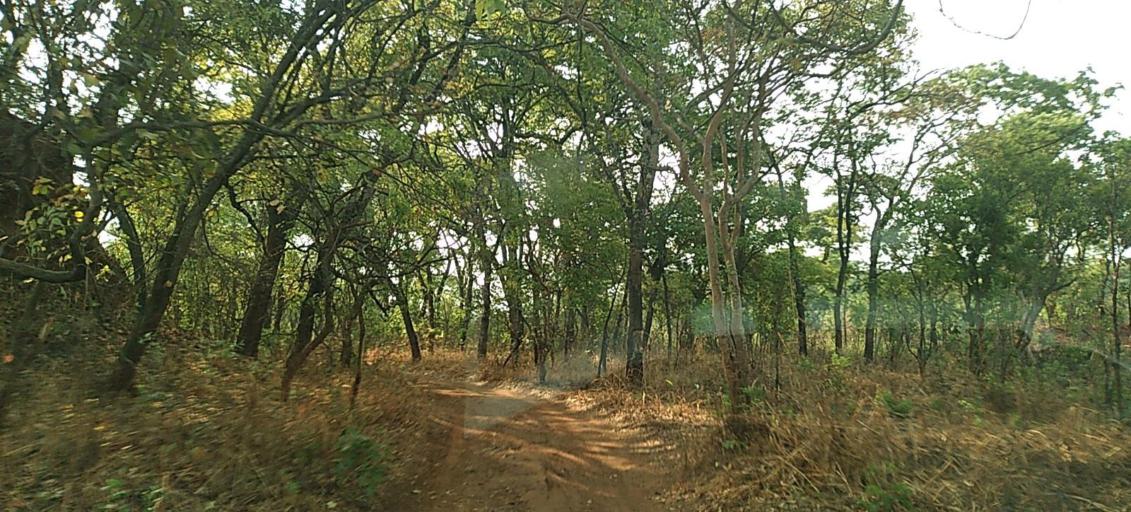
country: ZM
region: North-Western
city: Solwezi
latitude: -12.0587
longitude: 26.1637
